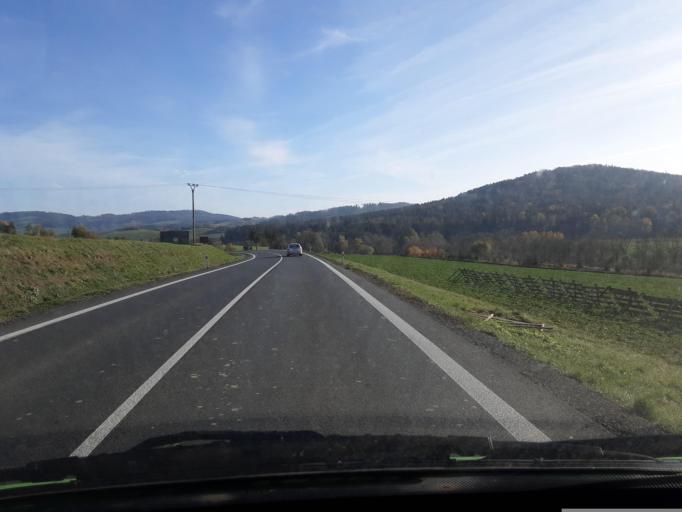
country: CZ
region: Plzensky
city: Klatovy
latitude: 49.3717
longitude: 13.3188
